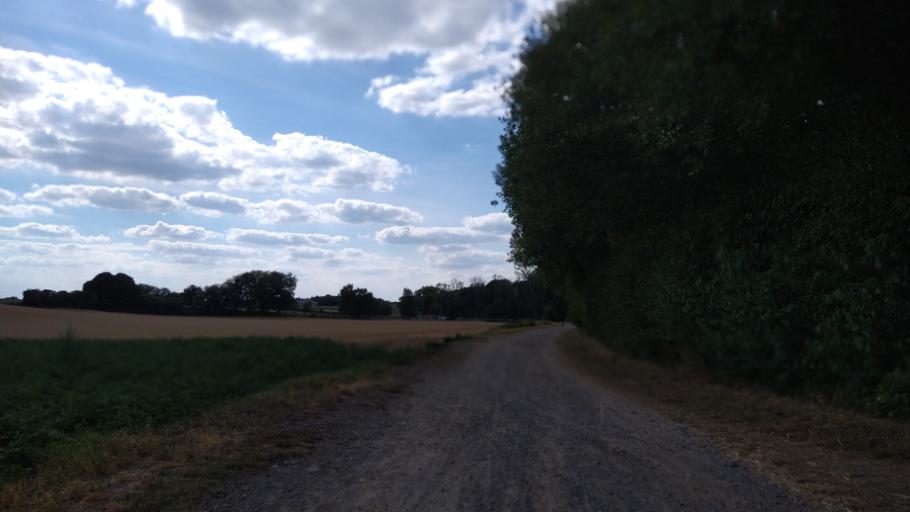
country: BE
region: Flanders
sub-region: Provincie Vlaams-Brabant
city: Kortenberg
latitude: 50.8652
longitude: 4.5338
